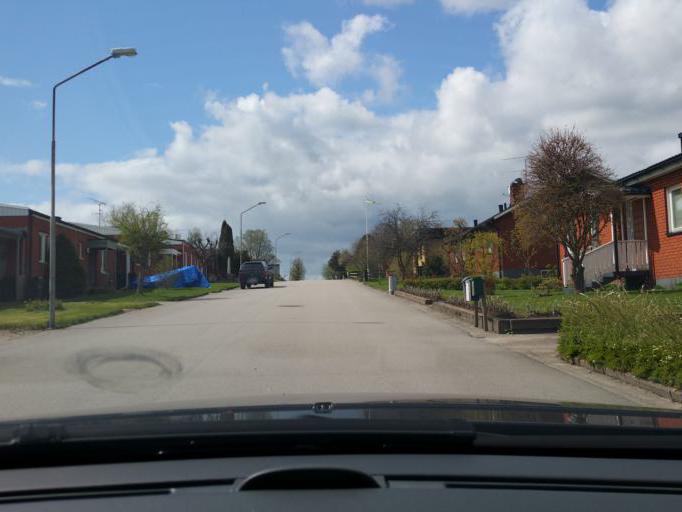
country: SE
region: Kronoberg
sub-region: Vaxjo Kommun
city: Lammhult
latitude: 57.1708
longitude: 14.5902
